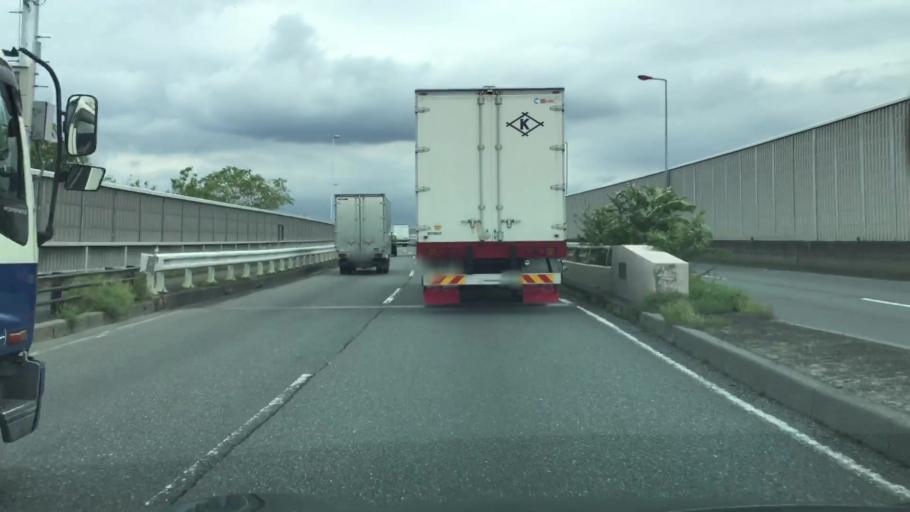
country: JP
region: Saitama
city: Kamifukuoka
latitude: 35.9129
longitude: 139.5349
